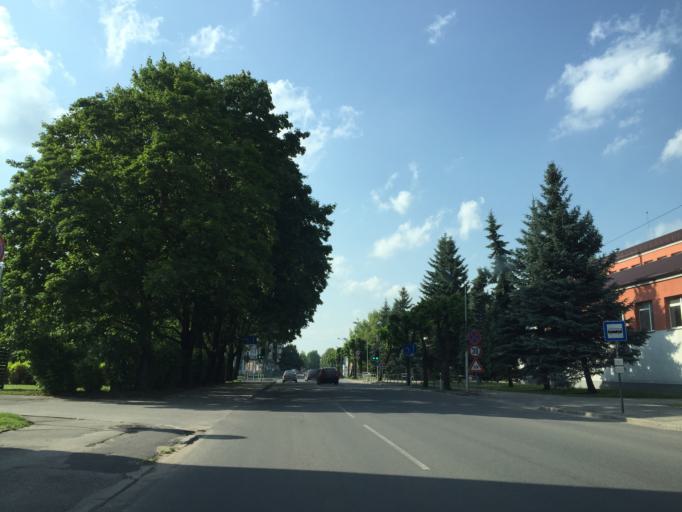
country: LV
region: Jelgava
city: Jelgava
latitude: 56.6541
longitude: 23.7240
